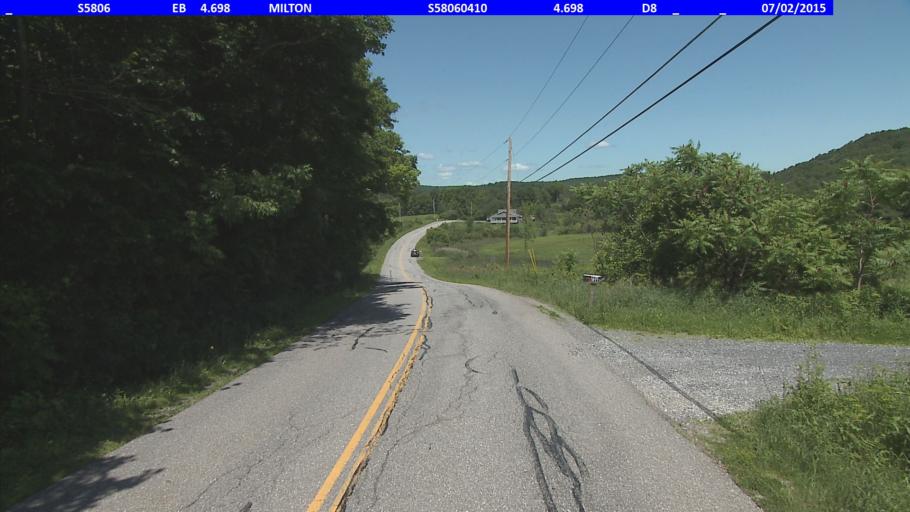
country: US
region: Vermont
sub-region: Chittenden County
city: Milton
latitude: 44.6885
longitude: -73.1772
